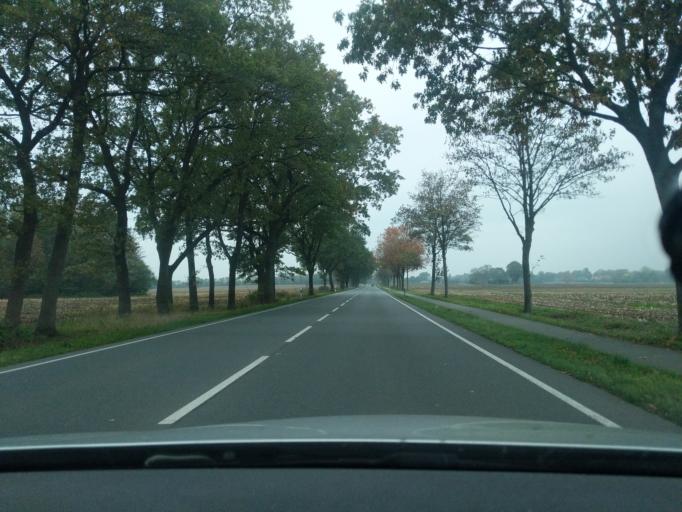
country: DE
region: Lower Saxony
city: Burweg
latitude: 53.6148
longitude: 9.2803
